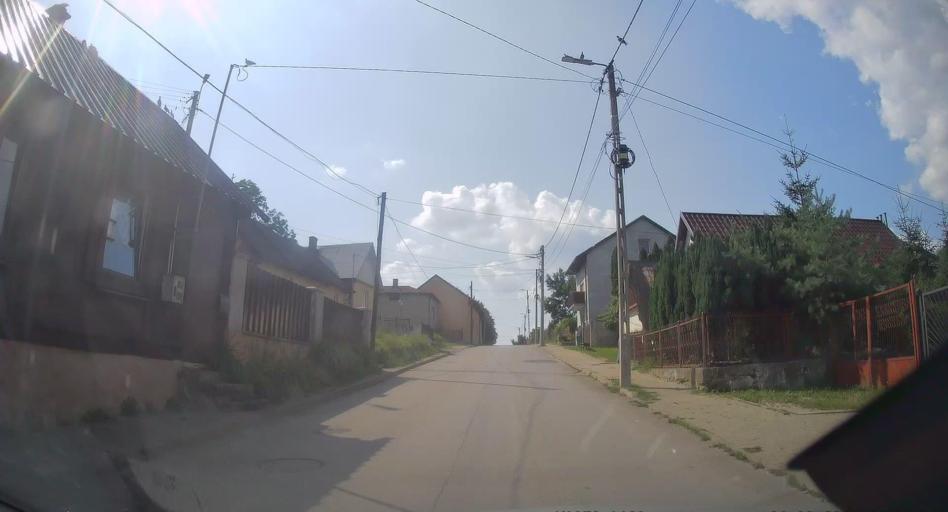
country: PL
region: Swietokrzyskie
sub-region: Powiat kielecki
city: Checiny
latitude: 50.8018
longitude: 20.4569
